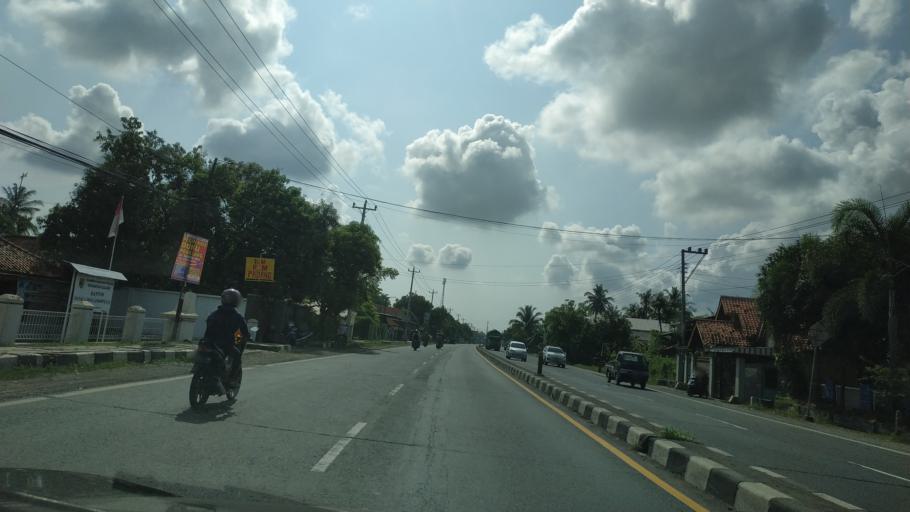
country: ID
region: Central Java
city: Comal
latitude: -6.8870
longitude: 109.5498
